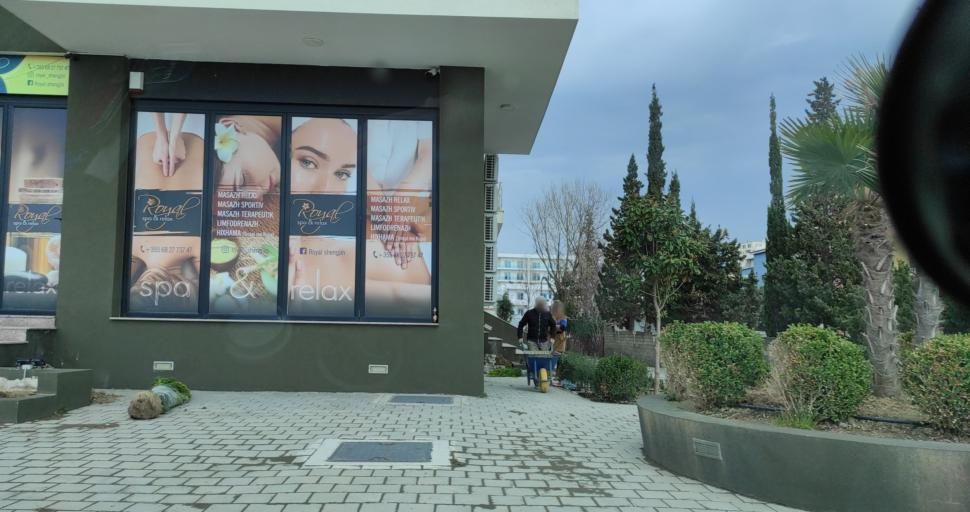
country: AL
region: Lezhe
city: Shengjin
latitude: 41.7964
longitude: 19.6019
